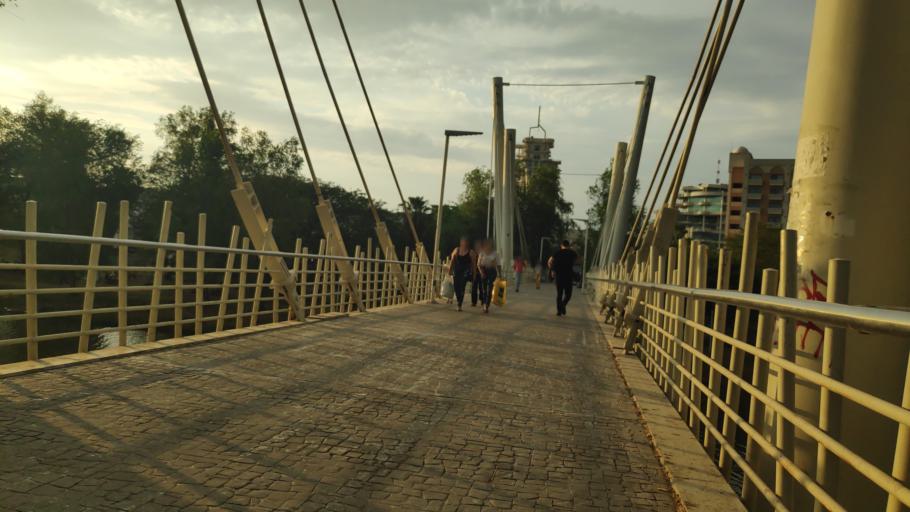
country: MX
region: Sinaloa
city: Culiacan
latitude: 24.8122
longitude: -107.3987
